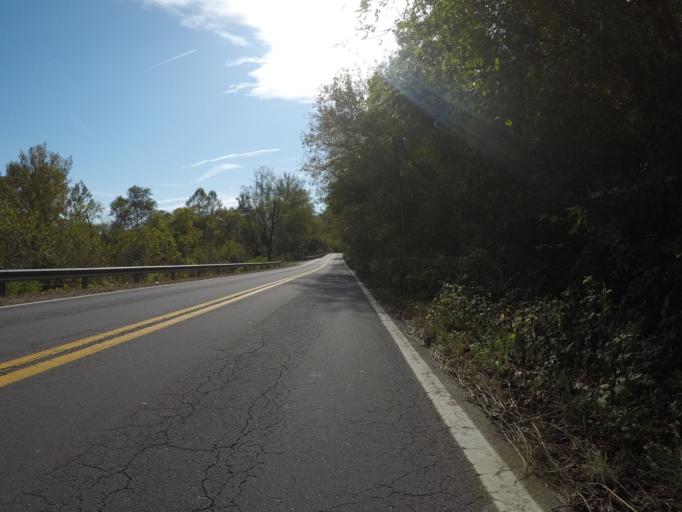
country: US
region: West Virginia
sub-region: Wayne County
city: Ceredo
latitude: 38.3713
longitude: -82.5463
